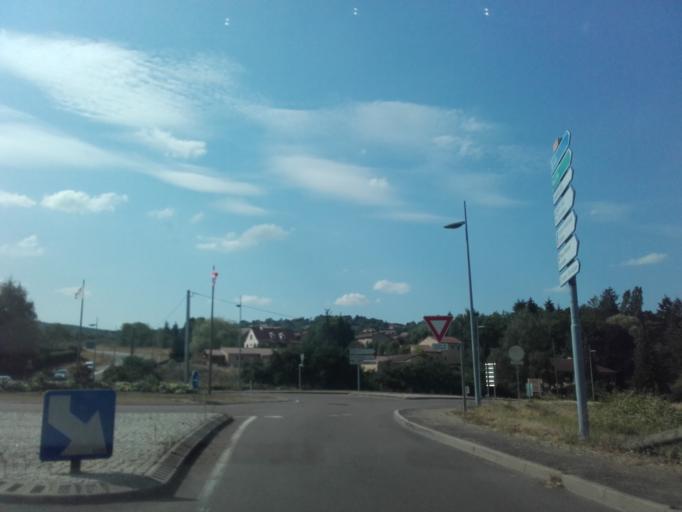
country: FR
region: Bourgogne
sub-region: Departement de Saone-et-Loire
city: Cluny
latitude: 46.4397
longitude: 4.6602
